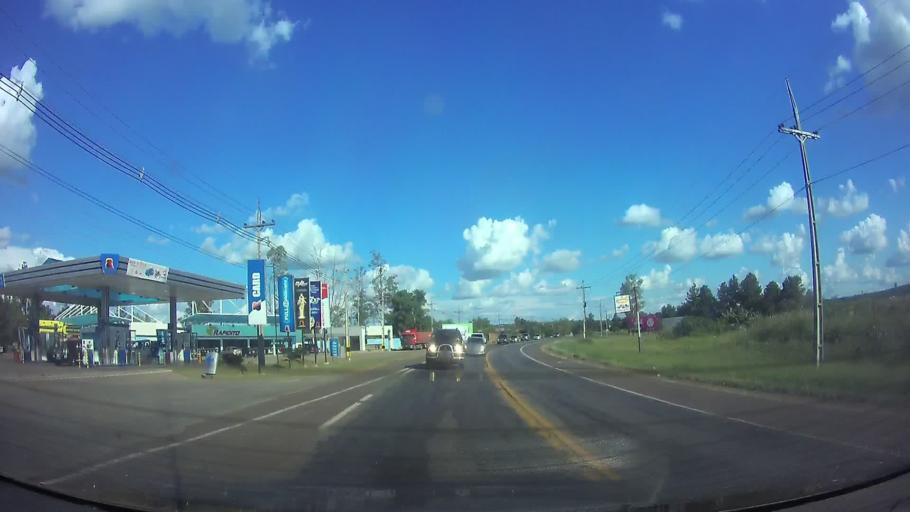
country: PY
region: Cordillera
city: Eusebio Ayala
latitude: -25.3831
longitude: -56.9719
